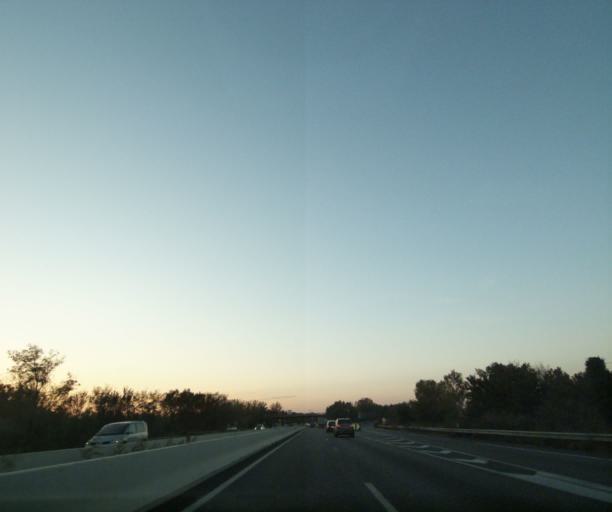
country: FR
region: Provence-Alpes-Cote d'Azur
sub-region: Departement des Bouches-du-Rhone
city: Arles
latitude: 43.6605
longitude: 4.6415
